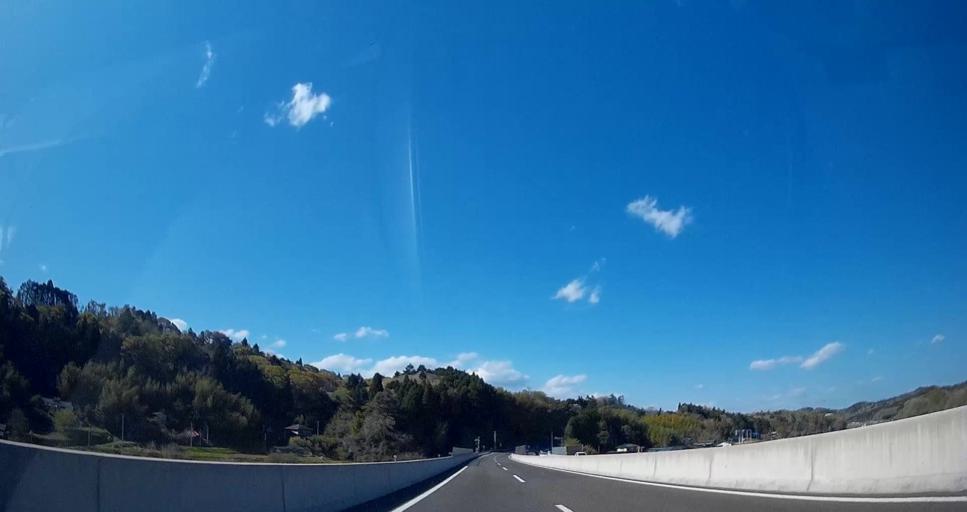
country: JP
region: Miyagi
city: Matsushima
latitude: 38.3835
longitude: 141.0341
